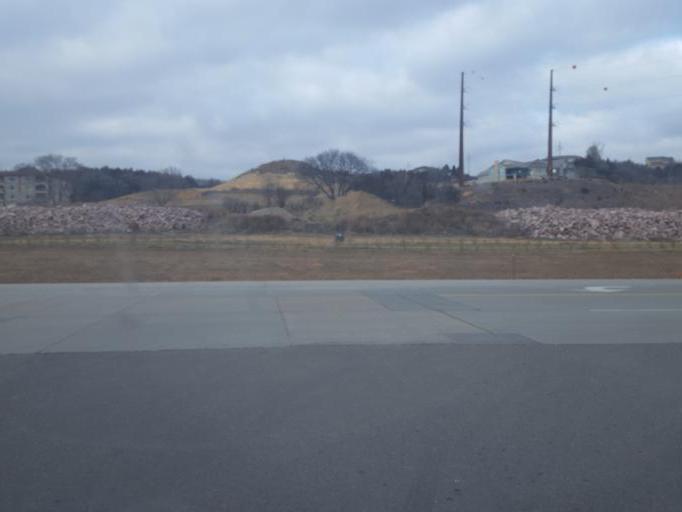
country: US
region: South Dakota
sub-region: Yankton County
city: Yankton
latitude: 42.8748
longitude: -97.4884
